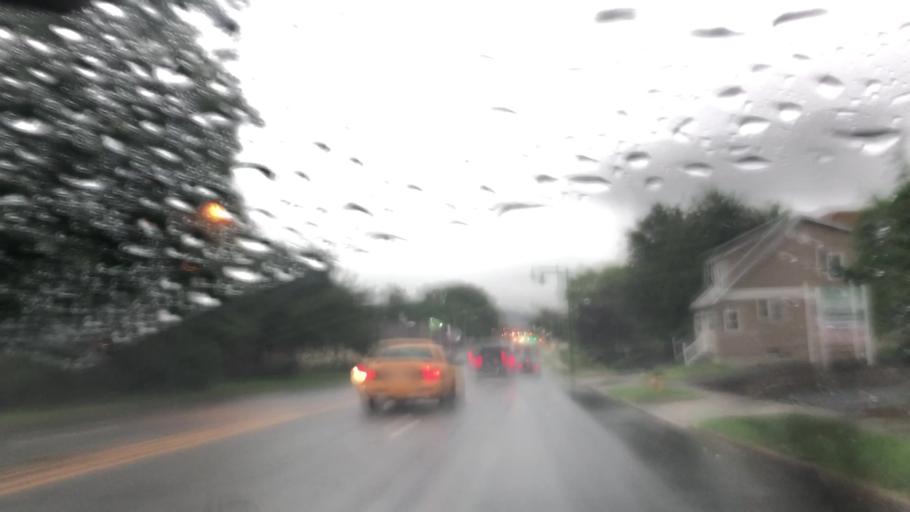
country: US
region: New Jersey
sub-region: Essex County
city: Glen Ridge
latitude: 40.8045
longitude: -74.2071
